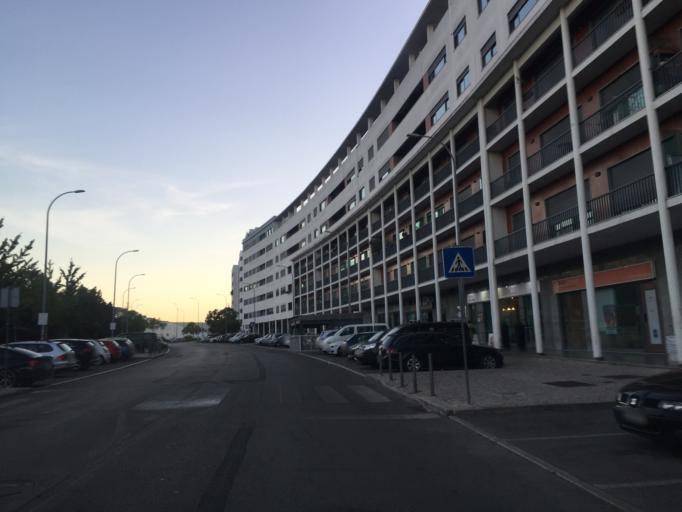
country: PT
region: Lisbon
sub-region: Odivelas
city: Odivelas
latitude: 38.7882
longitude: -9.1755
